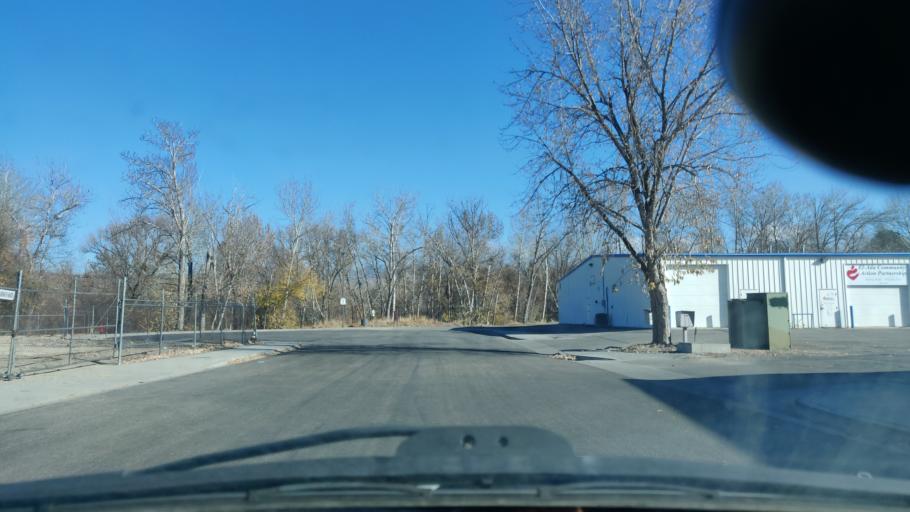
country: US
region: Idaho
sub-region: Ada County
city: Garden City
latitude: 43.6394
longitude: -116.2473
